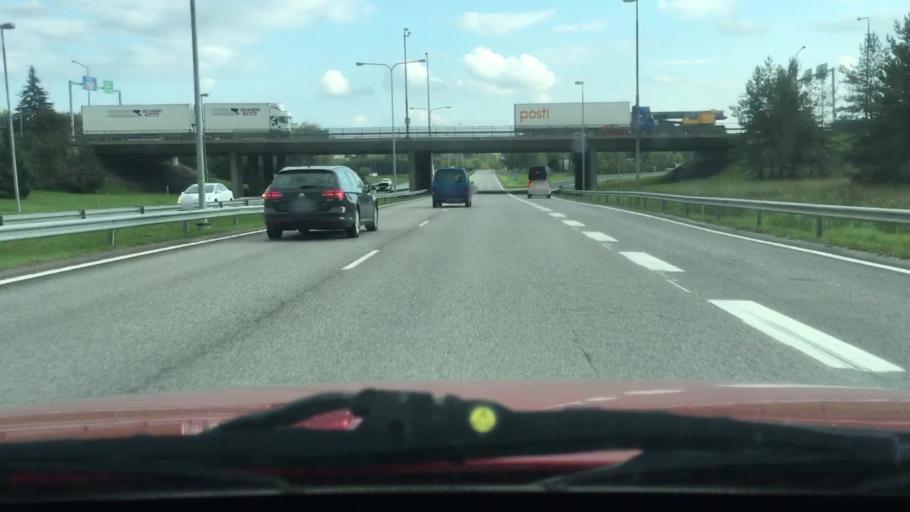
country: FI
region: Varsinais-Suomi
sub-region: Turku
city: Raisio
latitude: 60.4885
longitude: 22.1736
